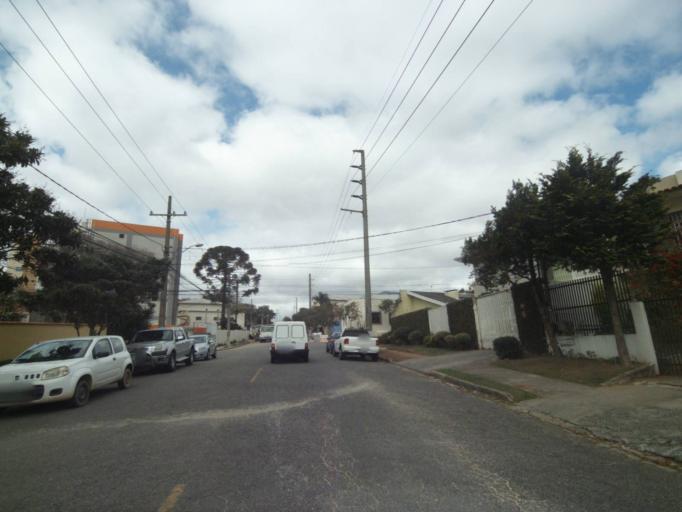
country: BR
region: Parana
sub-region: Curitiba
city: Curitiba
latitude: -25.4660
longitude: -49.2843
